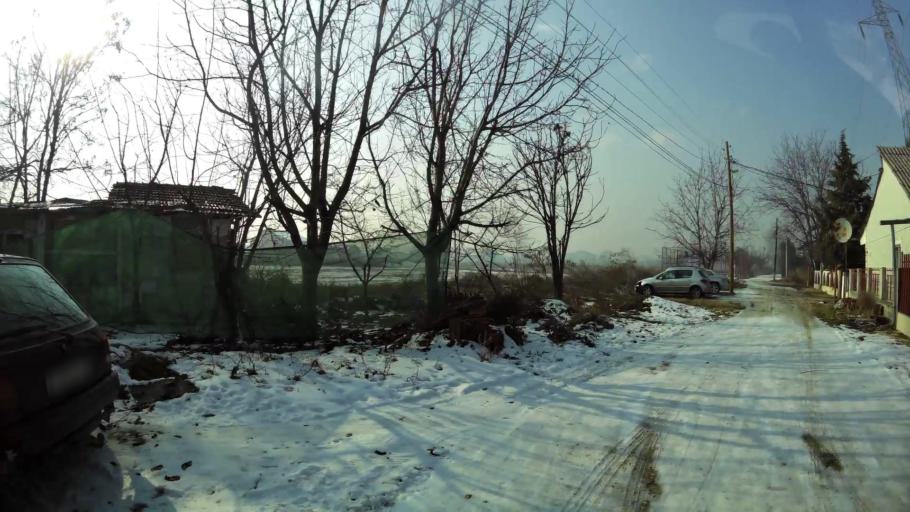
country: MK
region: Ilinden
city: Jurumleri
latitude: 41.9944
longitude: 21.5191
